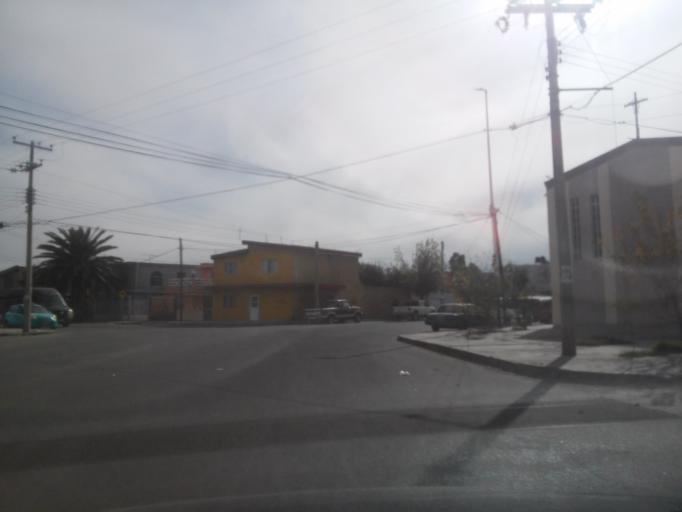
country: MX
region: Durango
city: Victoria de Durango
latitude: 24.0158
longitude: -104.6554
